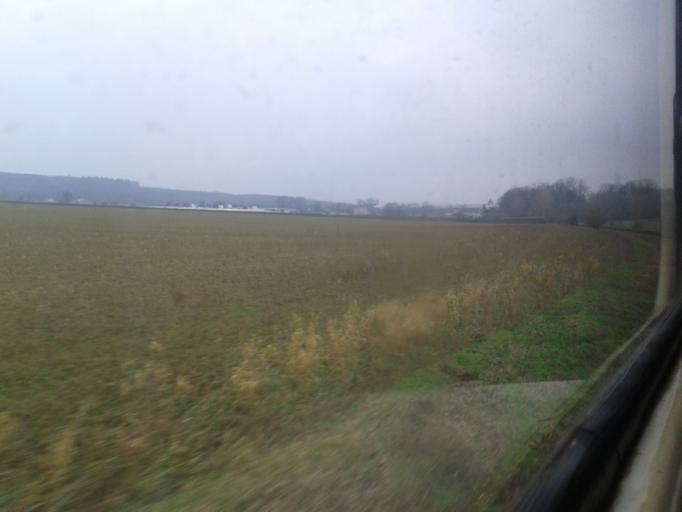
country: CZ
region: Olomoucky
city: Drahanovice
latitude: 49.5787
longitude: 17.0889
